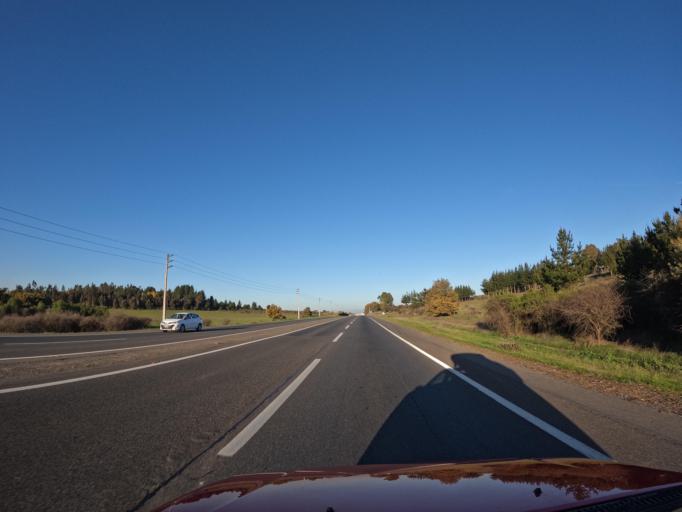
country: CL
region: Biobio
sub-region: Provincia de Nuble
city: Bulnes
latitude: -36.6588
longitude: -72.2925
